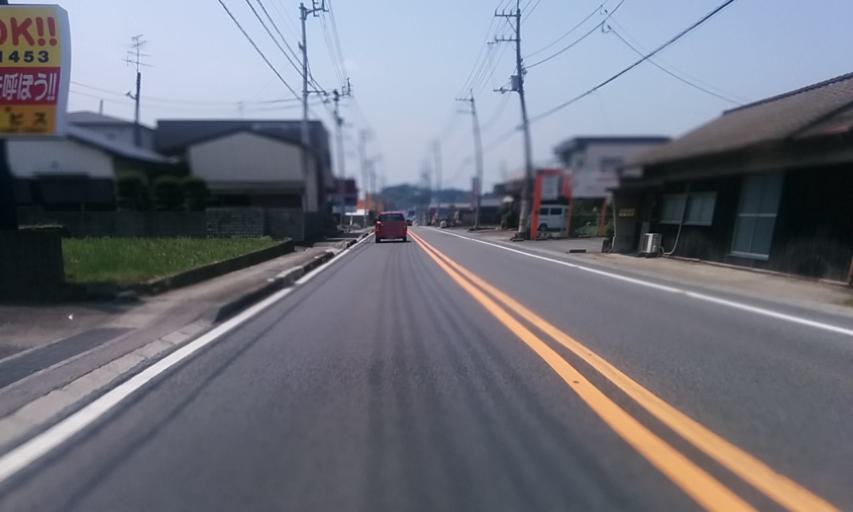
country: JP
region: Ehime
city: Niihama
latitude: 33.9292
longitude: 133.2720
